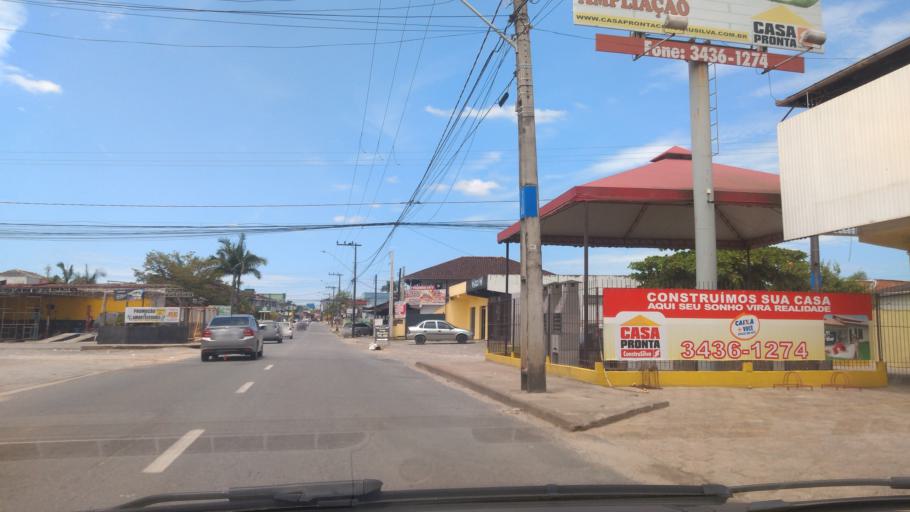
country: BR
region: Santa Catarina
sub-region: Joinville
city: Joinville
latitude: -26.3241
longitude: -48.8118
